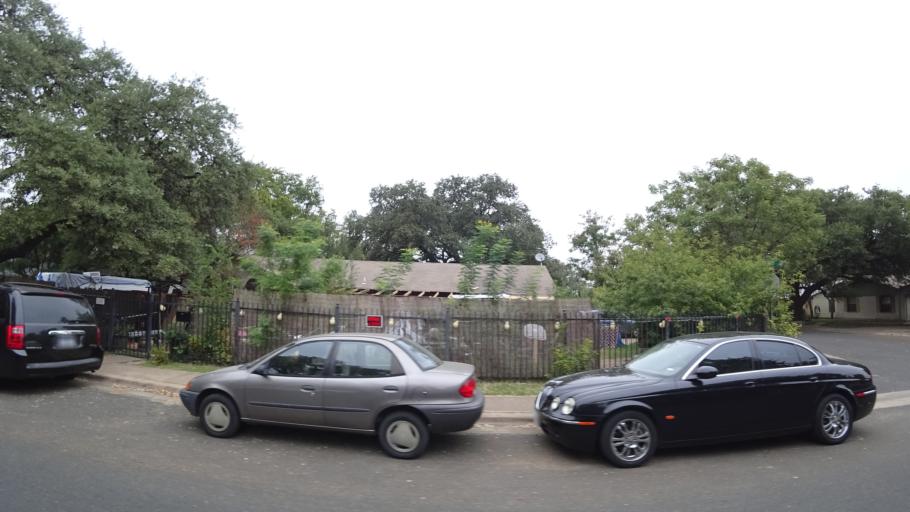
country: US
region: Texas
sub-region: Travis County
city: Onion Creek
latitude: 30.2028
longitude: -97.7806
